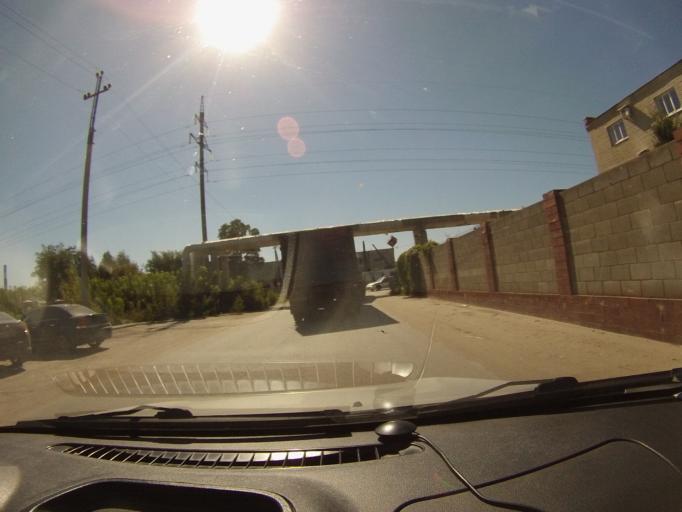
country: RU
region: Tambov
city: Donskoye
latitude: 52.7571
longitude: 41.4618
